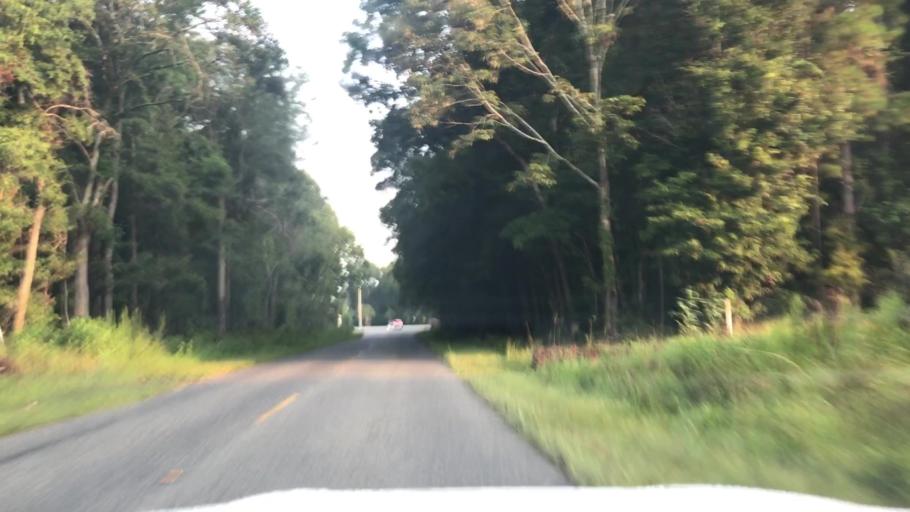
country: US
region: South Carolina
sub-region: Charleston County
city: Shell Point
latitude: 32.8180
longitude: -80.0912
